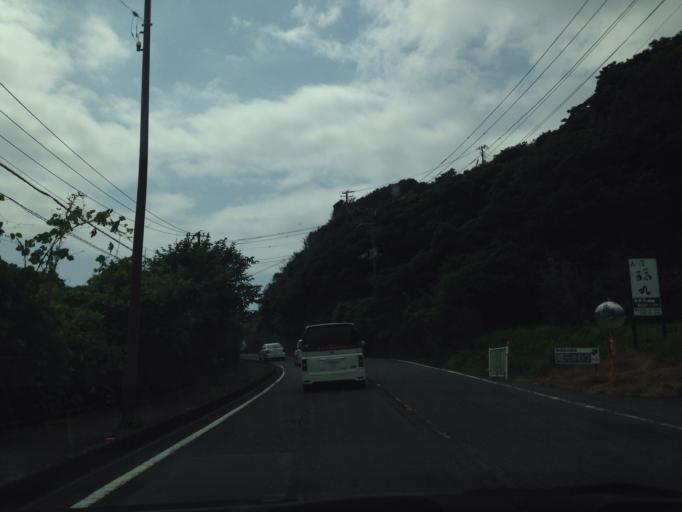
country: JP
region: Shizuoka
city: Shimoda
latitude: 34.7373
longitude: 138.9996
